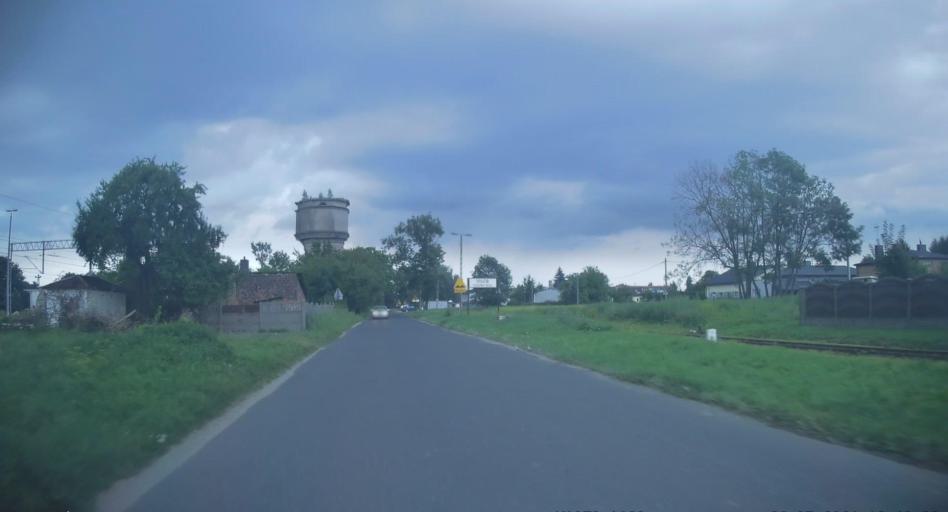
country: PL
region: Lodz Voivodeship
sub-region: Powiat brzezinski
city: Rogow
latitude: 51.8160
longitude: 19.8839
